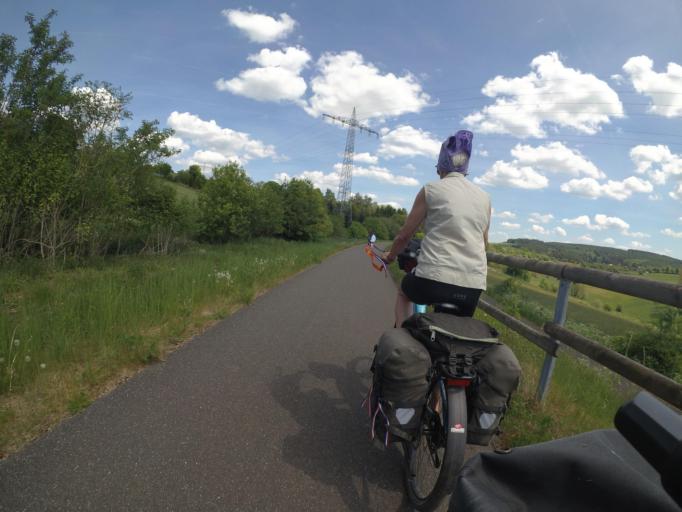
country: DE
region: Rheinland-Pfalz
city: Scheid
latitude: 50.3543
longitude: 6.4246
